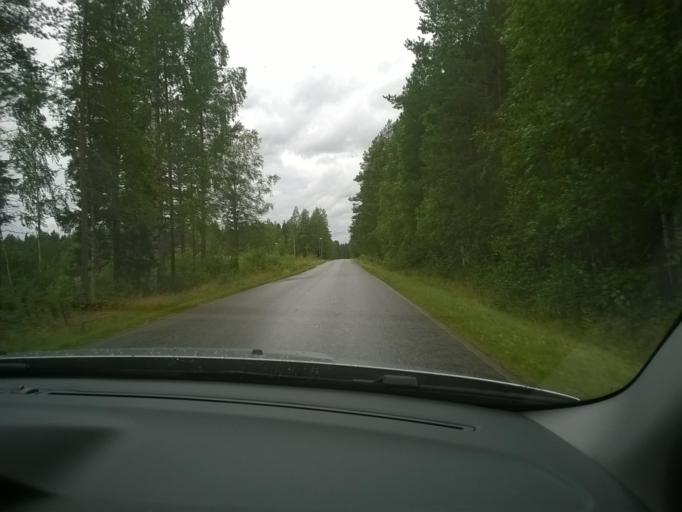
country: FI
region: Kainuu
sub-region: Kehys-Kainuu
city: Kuhmo
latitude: 64.1346
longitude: 29.4314
